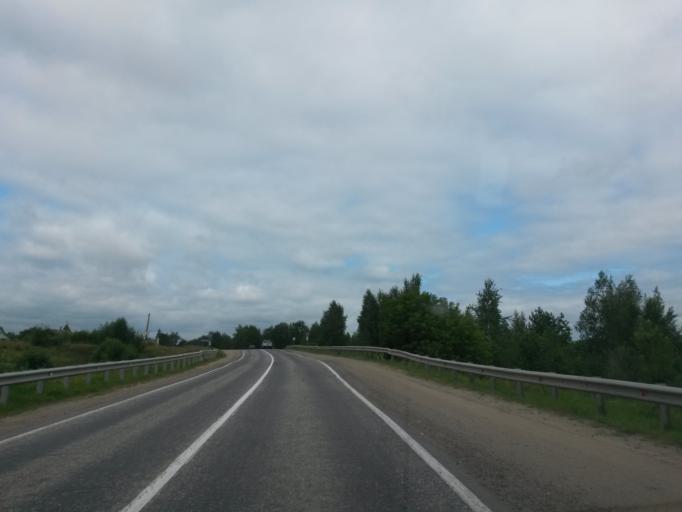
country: RU
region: Jaroslavl
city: Yaroslavl
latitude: 57.5140
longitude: 39.8964
